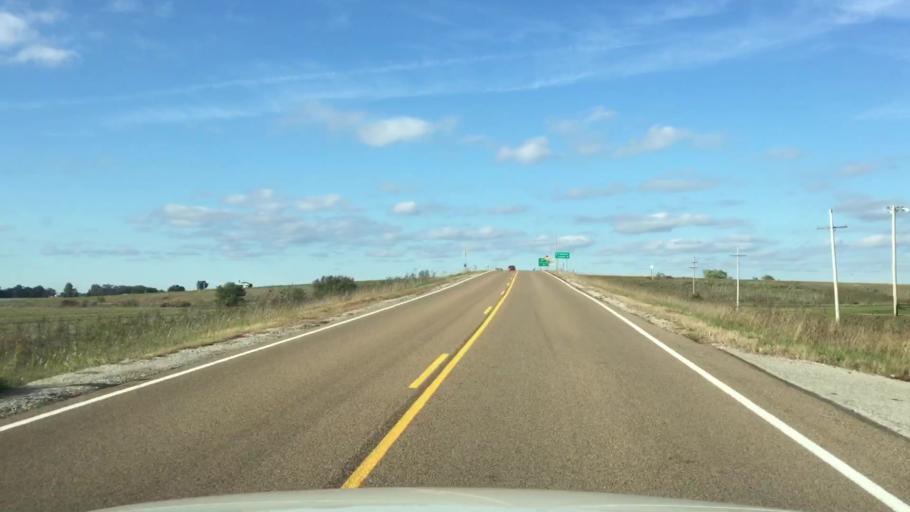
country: US
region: Kansas
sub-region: Douglas County
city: Eudora
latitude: 38.9320
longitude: -95.1489
